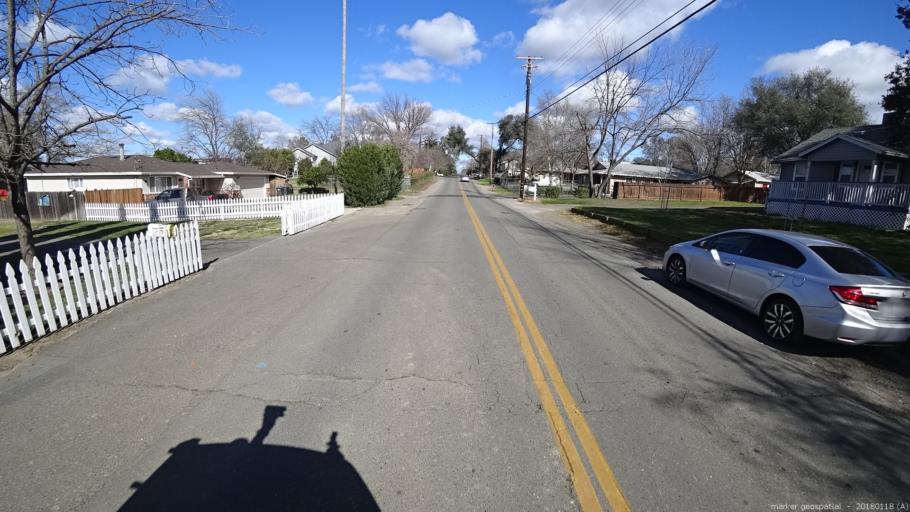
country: US
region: California
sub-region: Sacramento County
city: Orangevale
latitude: 38.6864
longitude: -121.2067
